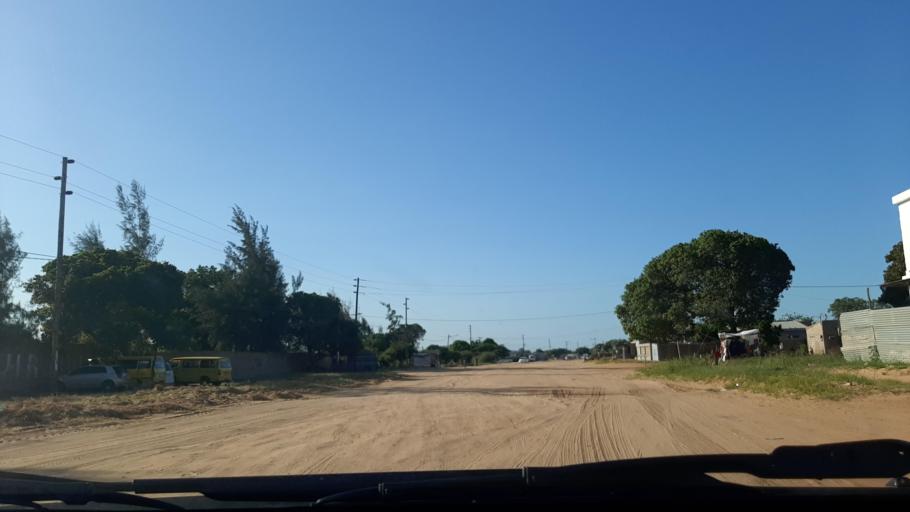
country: MZ
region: Maputo City
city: Maputo
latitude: -25.7910
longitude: 32.5523
